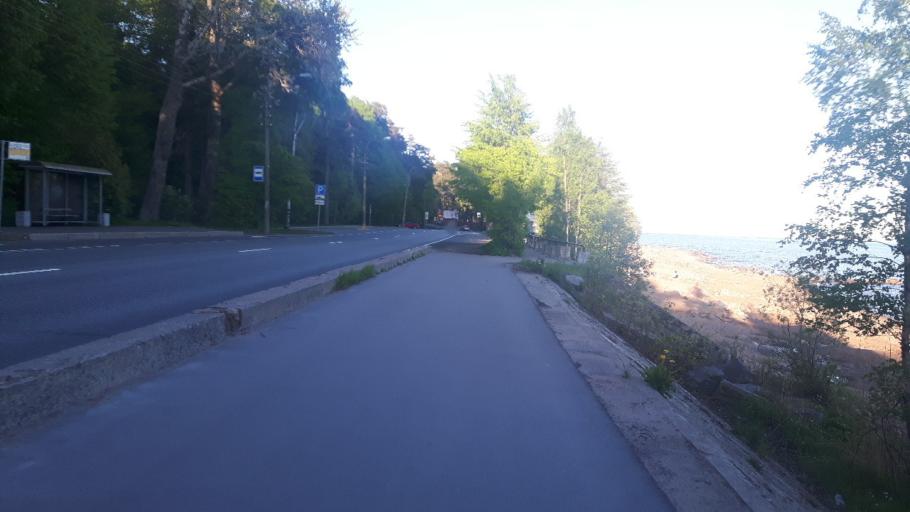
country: RU
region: St.-Petersburg
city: Zelenogorsk
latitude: 60.1915
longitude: 29.6448
